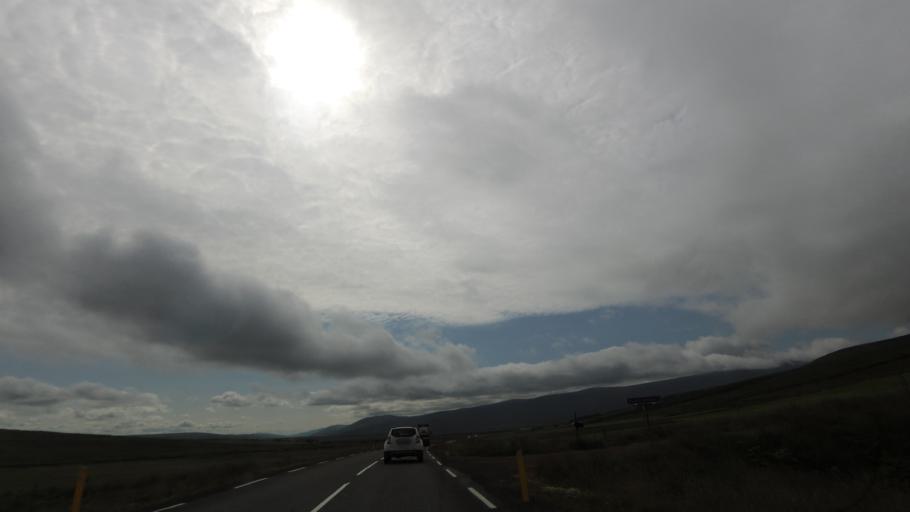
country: IS
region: Northeast
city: Laugar
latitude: 65.7351
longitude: -17.5908
